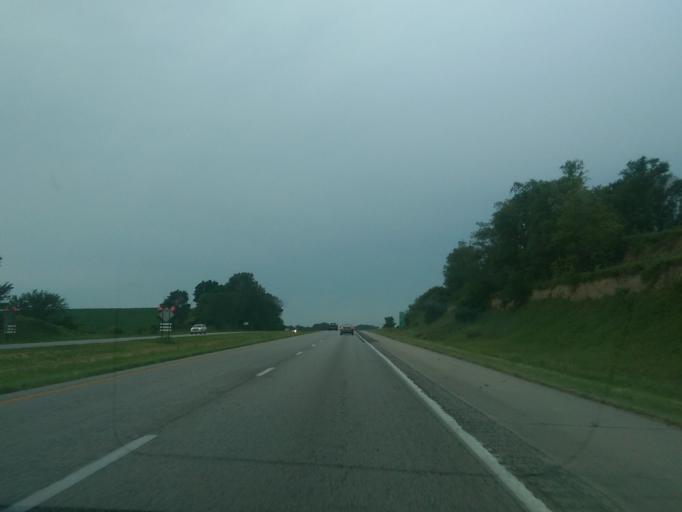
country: US
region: Missouri
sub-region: Holt County
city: Oregon
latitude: 40.0607
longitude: -95.1669
